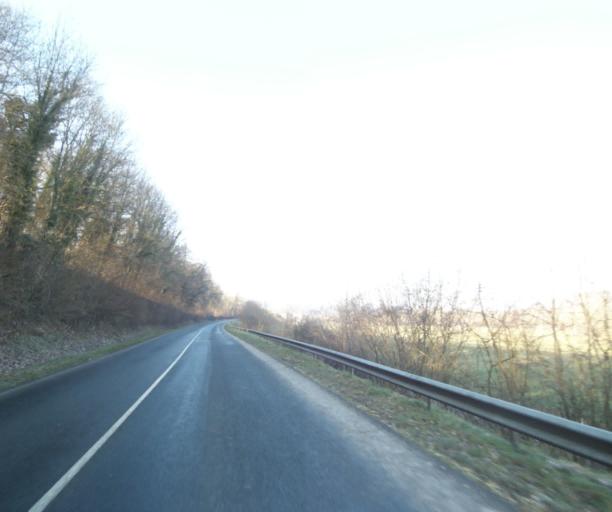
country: FR
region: Champagne-Ardenne
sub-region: Departement de la Haute-Marne
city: Chevillon
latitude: 48.5188
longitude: 5.1080
